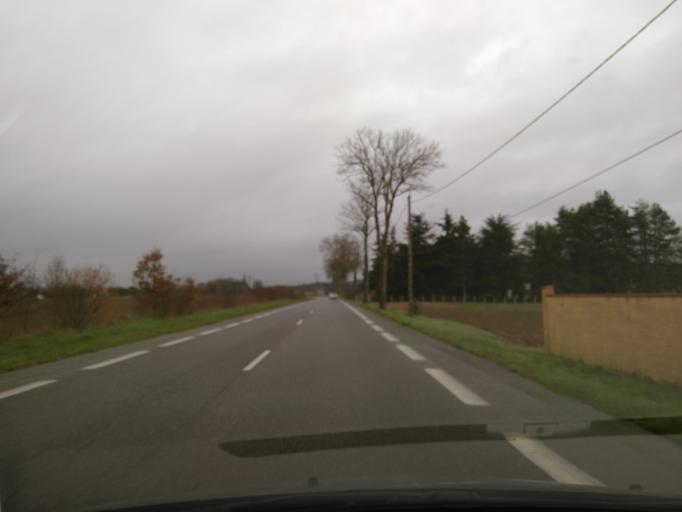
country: FR
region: Midi-Pyrenees
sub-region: Departement de la Haute-Garonne
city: Carbonne
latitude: 43.2807
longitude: 1.2127
